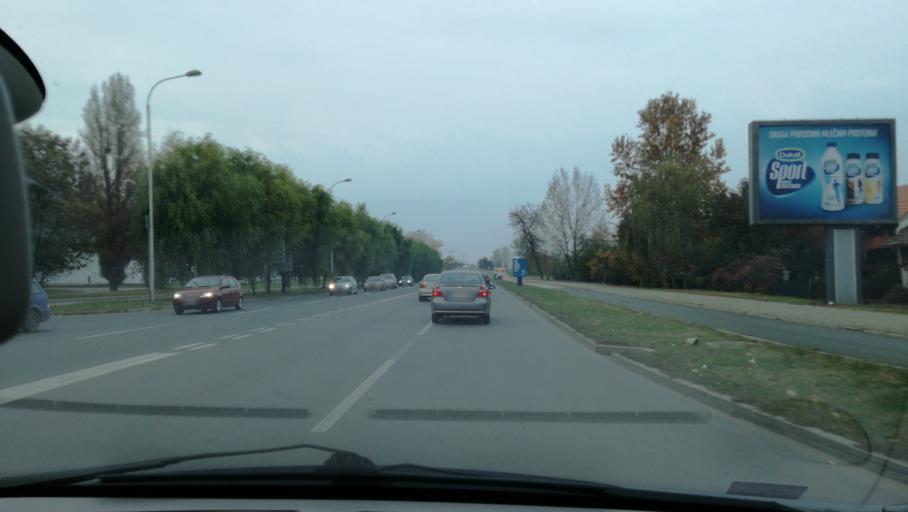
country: RS
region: Autonomna Pokrajina Vojvodina
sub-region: Juznobacki Okrug
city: Novi Sad
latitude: 45.2737
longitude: 19.8302
